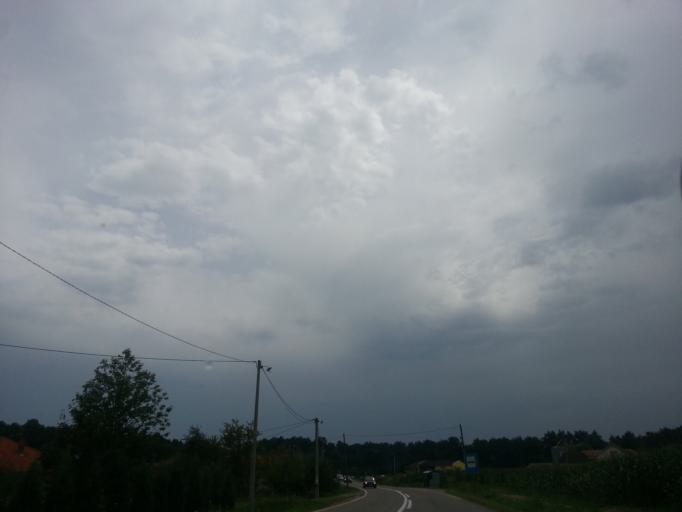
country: BA
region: Republika Srpska
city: Velika Obarska
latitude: 44.8007
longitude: 19.0816
